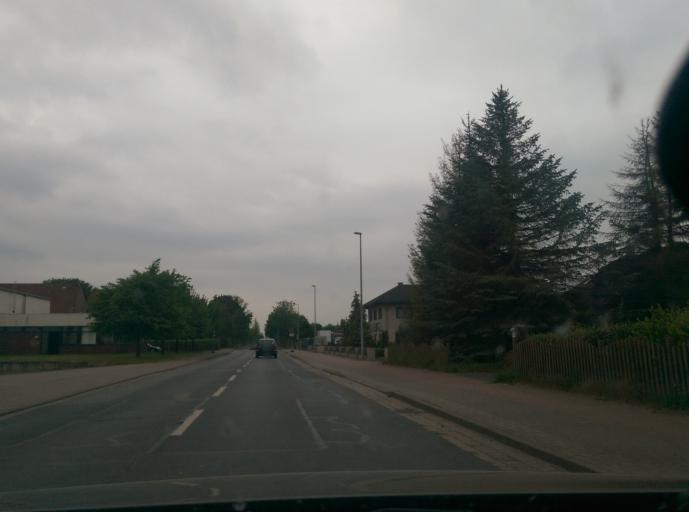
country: DE
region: Lower Saxony
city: Garbsen-Mitte
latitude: 52.4467
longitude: 9.6021
